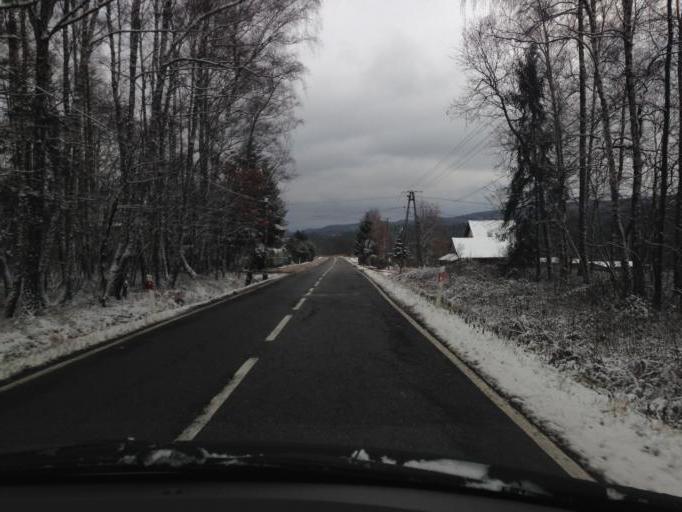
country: PL
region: Lesser Poland Voivodeship
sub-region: Powiat bochenski
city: Nowy Wisnicz
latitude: 49.8496
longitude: 20.4968
